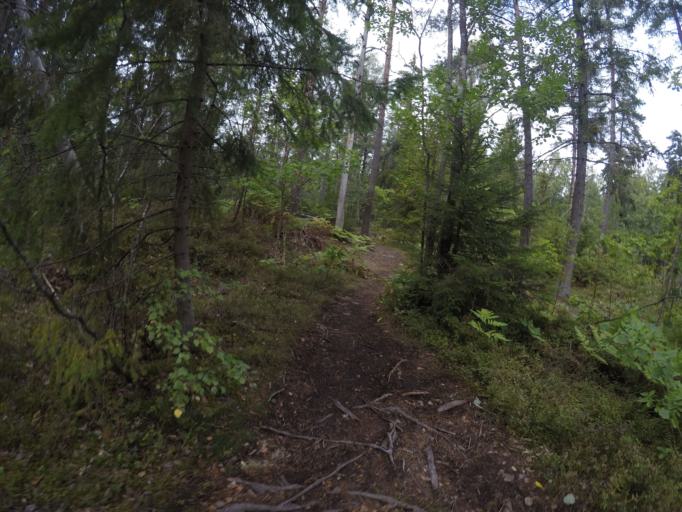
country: SE
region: Vaestmanland
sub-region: Vasteras
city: Vasteras
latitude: 59.6488
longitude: 16.5137
